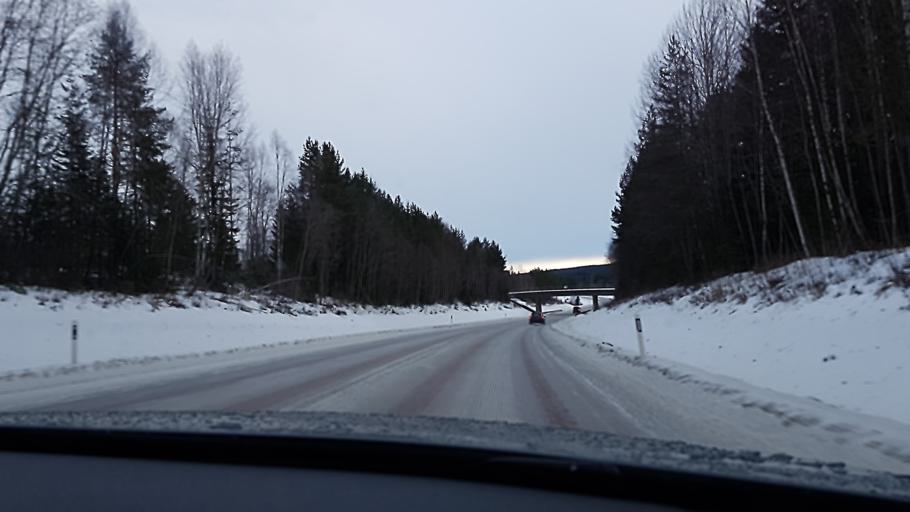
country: SE
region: Jaemtland
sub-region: Bergs Kommun
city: Hoverberg
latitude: 62.7564
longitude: 14.4359
